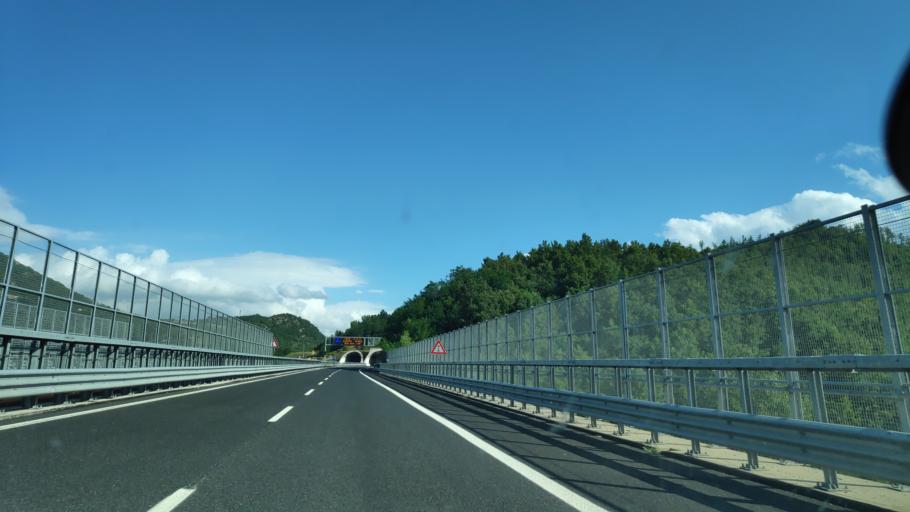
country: IT
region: Campania
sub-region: Provincia di Salerno
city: Casalbuono
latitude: 40.2306
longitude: 15.6673
